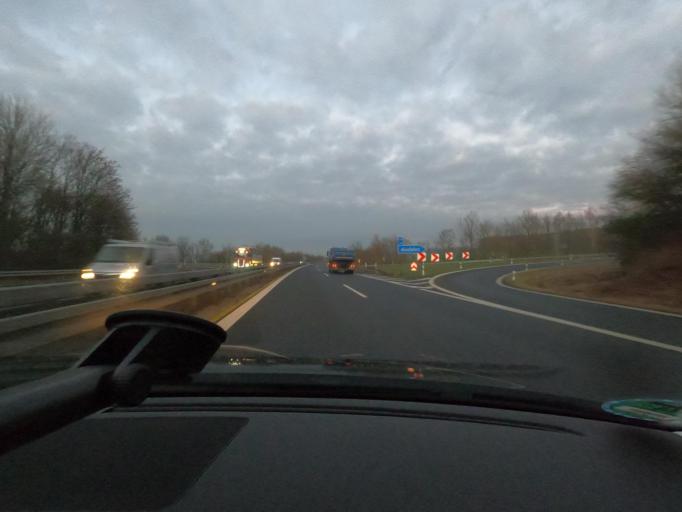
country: DE
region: Bavaria
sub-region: Upper Franconia
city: Ebensfeld
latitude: 50.0597
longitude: 10.9673
